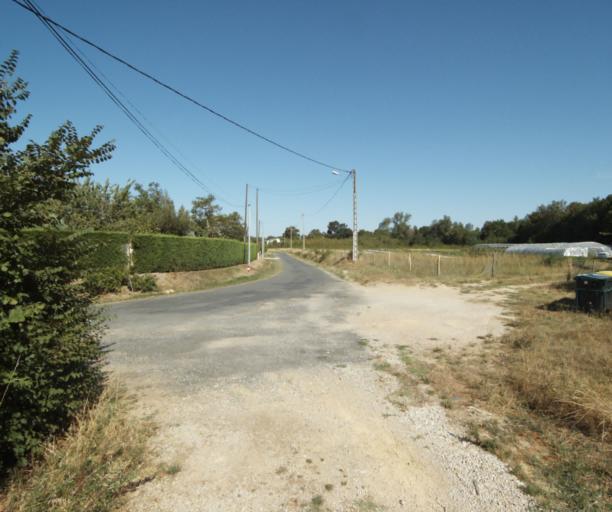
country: FR
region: Midi-Pyrenees
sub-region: Departement du Tarn
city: Soreze
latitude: 43.4541
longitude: 2.0404
